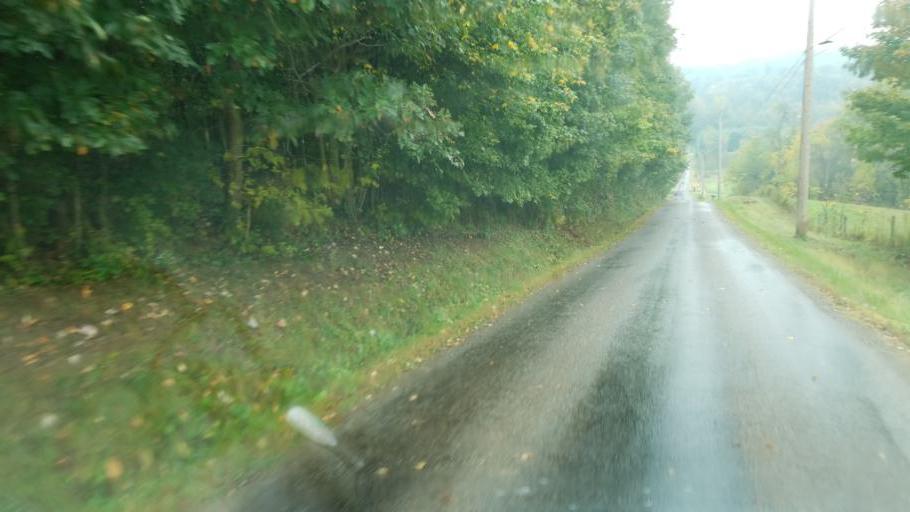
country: US
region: Ohio
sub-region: Sandusky County
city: Bellville
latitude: 40.6754
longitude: -82.3858
